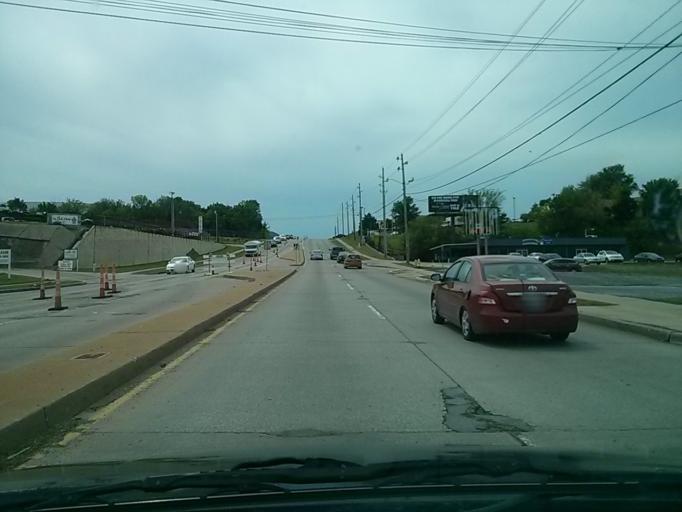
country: US
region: Oklahoma
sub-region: Tulsa County
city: Jenks
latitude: 36.0749
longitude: -95.9043
